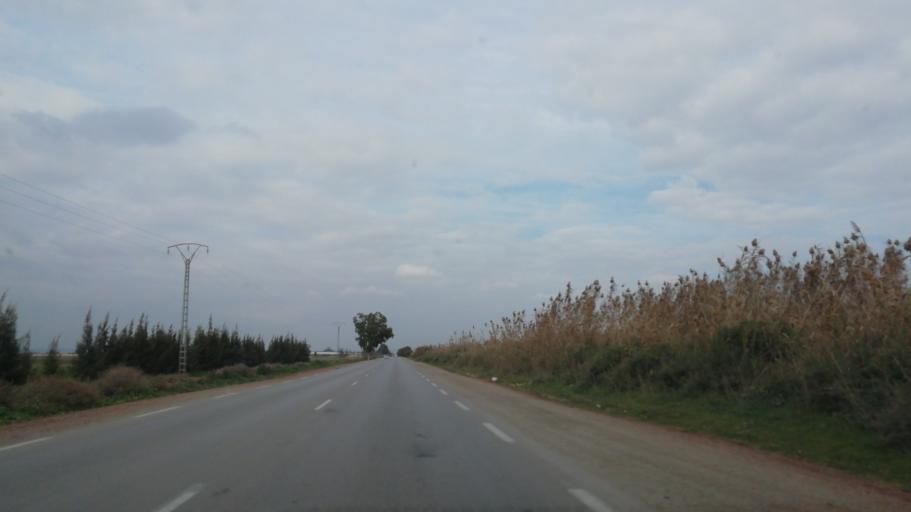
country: DZ
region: Mascara
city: Mascara
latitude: 35.6445
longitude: 0.0601
